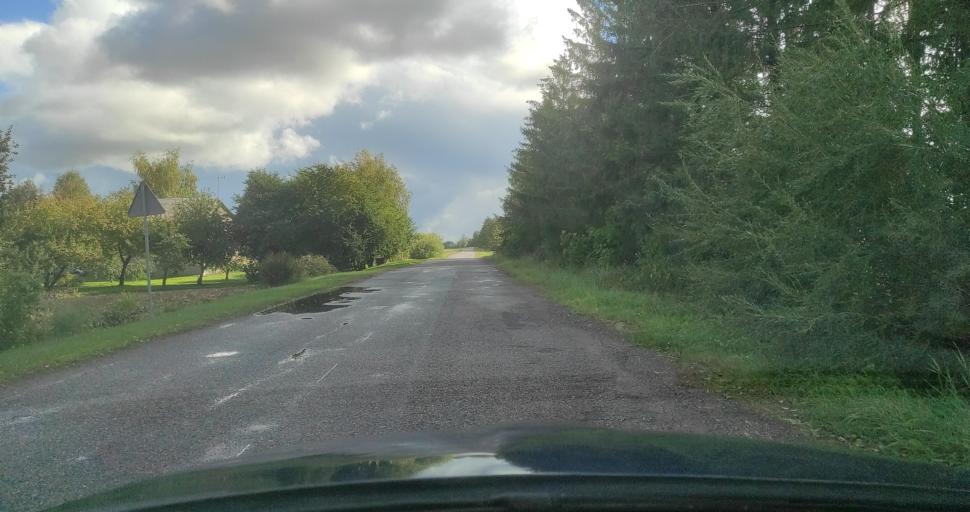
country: LV
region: Ventspils Rajons
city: Piltene
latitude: 57.2644
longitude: 21.5912
